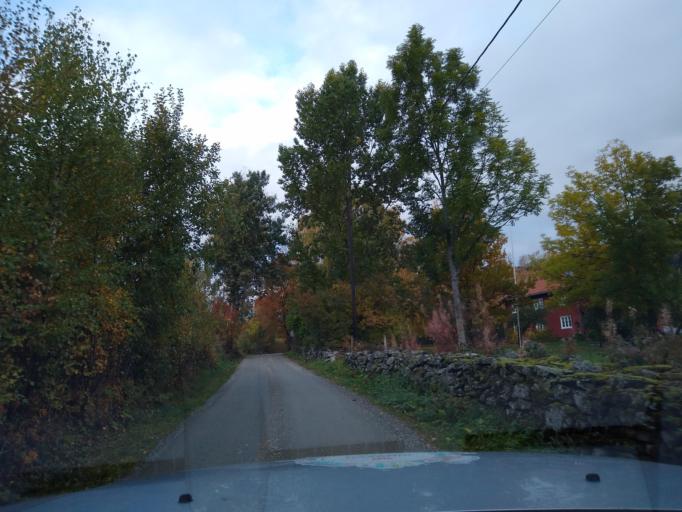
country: NO
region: Oppland
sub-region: Ringebu
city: Ringebu
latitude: 61.5413
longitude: 10.1297
